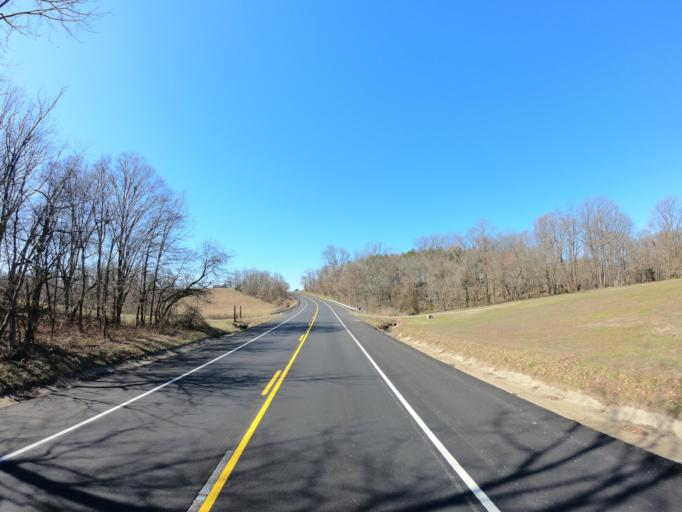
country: US
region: Delaware
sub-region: New Castle County
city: Townsend
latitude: 39.3644
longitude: -75.8190
